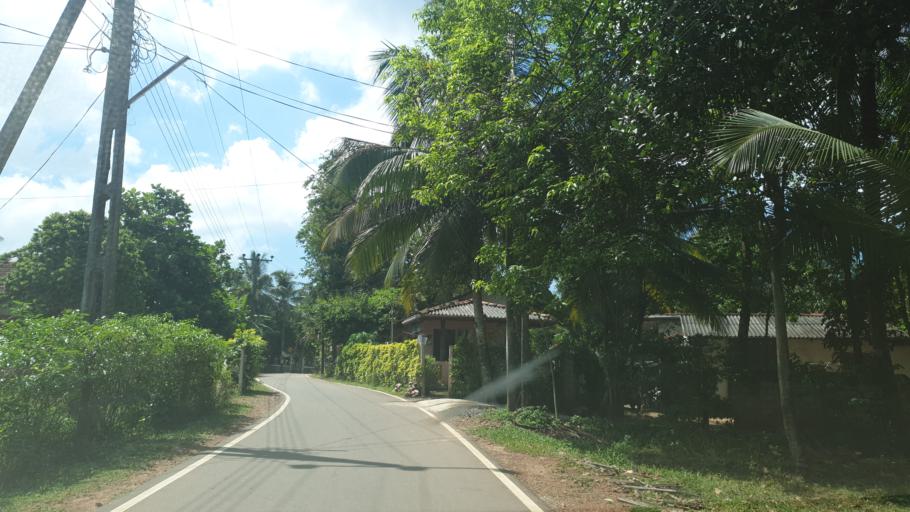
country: LK
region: Western
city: Panadura
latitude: 6.6766
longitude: 79.9696
